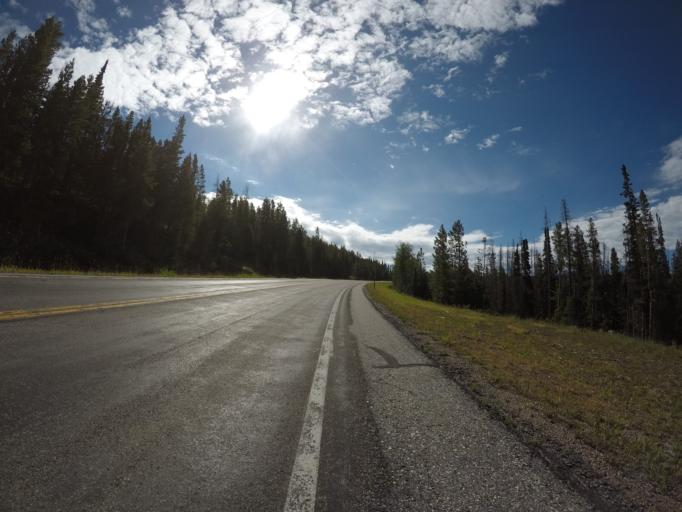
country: US
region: Wyoming
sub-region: Carbon County
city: Saratoga
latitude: 41.3295
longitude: -106.4769
